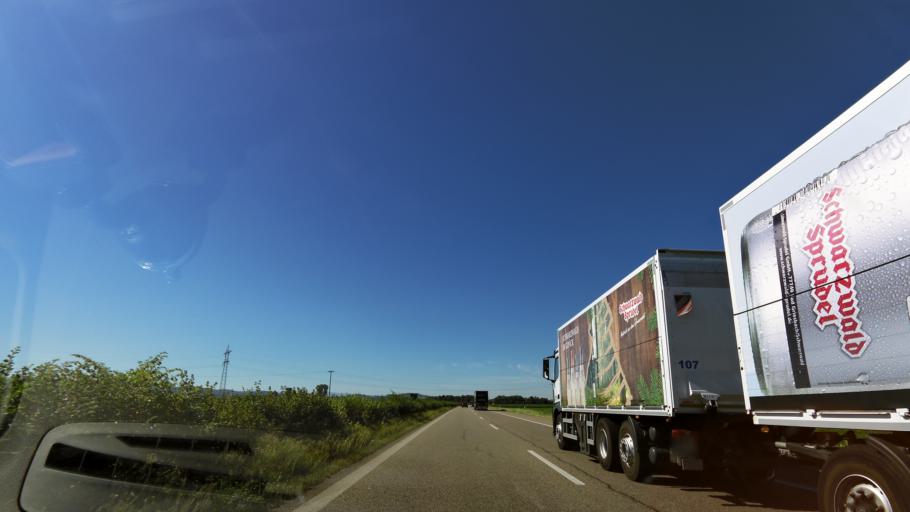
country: DE
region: Baden-Wuerttemberg
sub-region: Freiburg Region
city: Mahlberg
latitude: 48.3029
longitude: 7.7899
